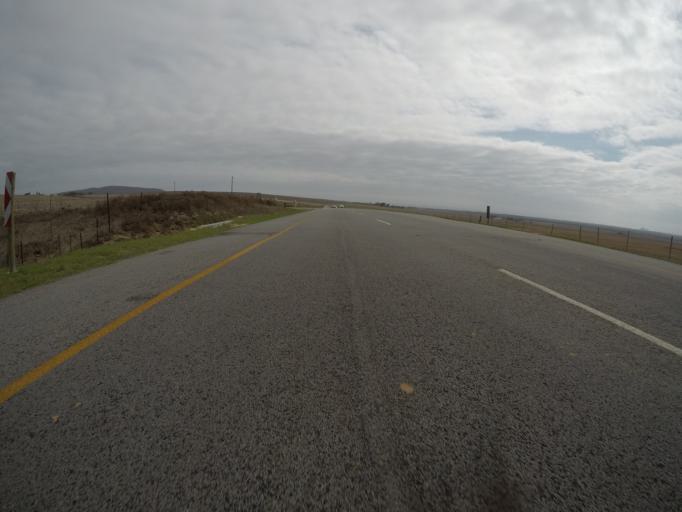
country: ZA
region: Western Cape
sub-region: City of Cape Town
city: Sunset Beach
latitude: -33.7253
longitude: 18.4904
